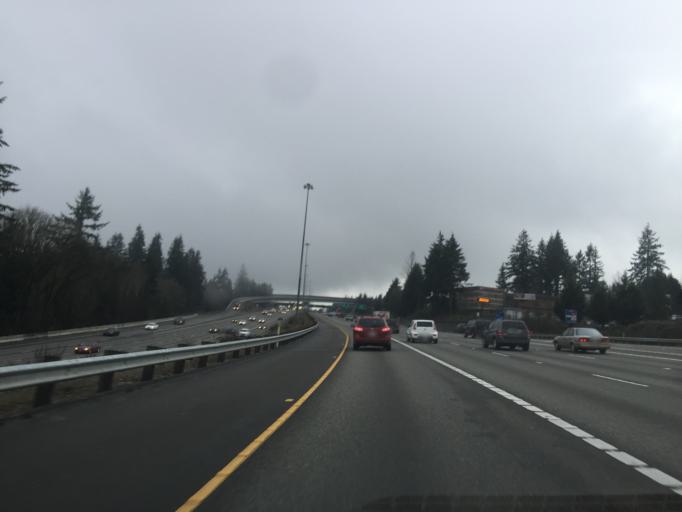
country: US
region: Washington
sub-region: Snohomish County
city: Everett
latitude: 47.9259
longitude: -122.2036
